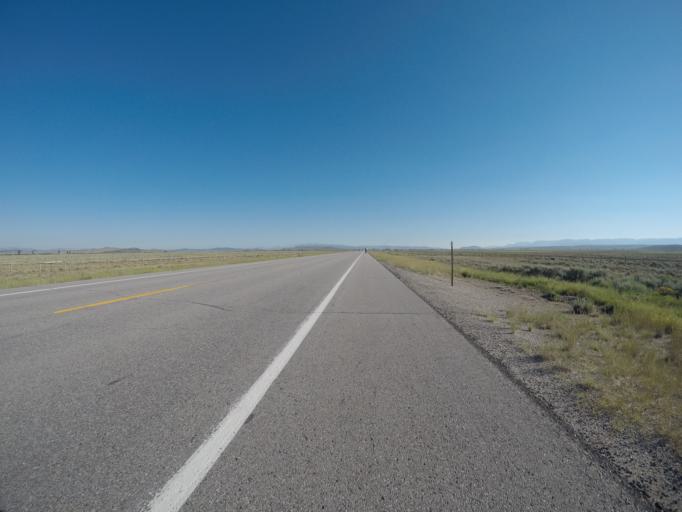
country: US
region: Wyoming
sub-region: Sublette County
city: Pinedale
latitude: 42.9570
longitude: -110.0872
